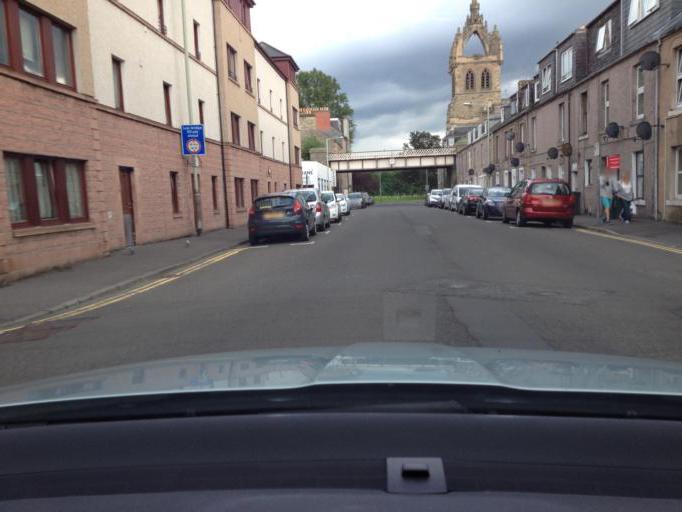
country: GB
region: Scotland
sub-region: Perth and Kinross
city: Perth
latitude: 56.3934
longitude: -3.4323
